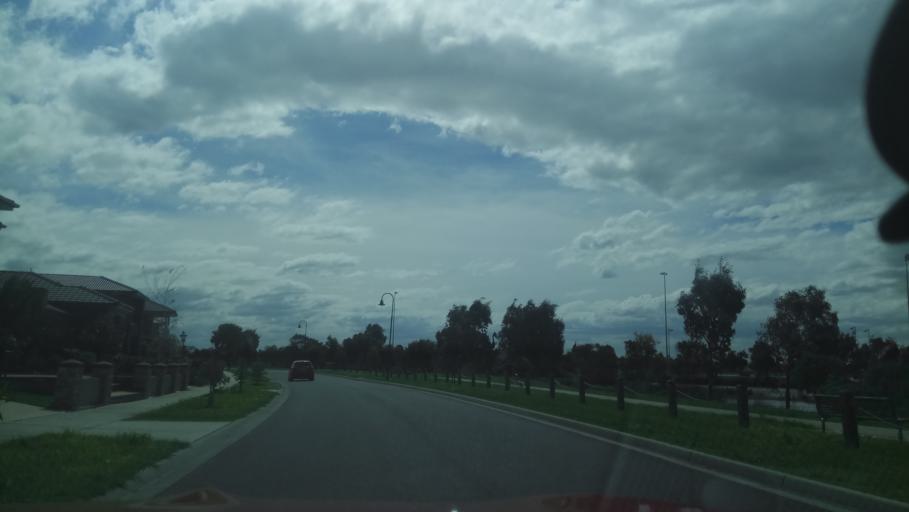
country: AU
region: Victoria
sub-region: Casey
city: Lynbrook
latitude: -38.0752
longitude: 145.2507
